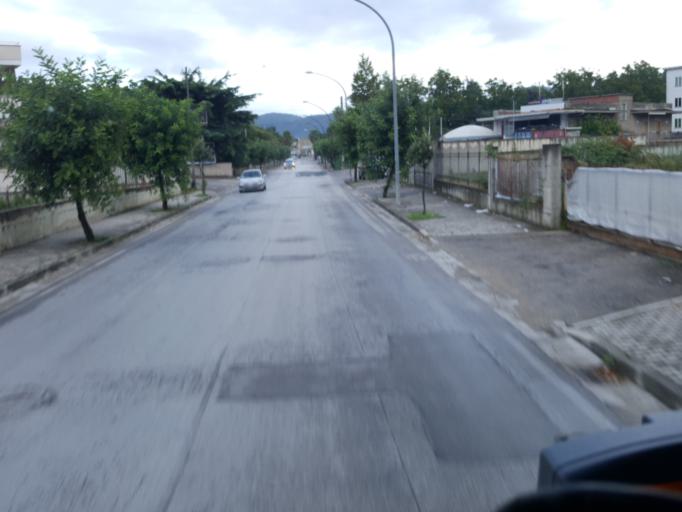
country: IT
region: Campania
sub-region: Provincia di Napoli
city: Palma Campania
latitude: 40.8747
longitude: 14.5495
